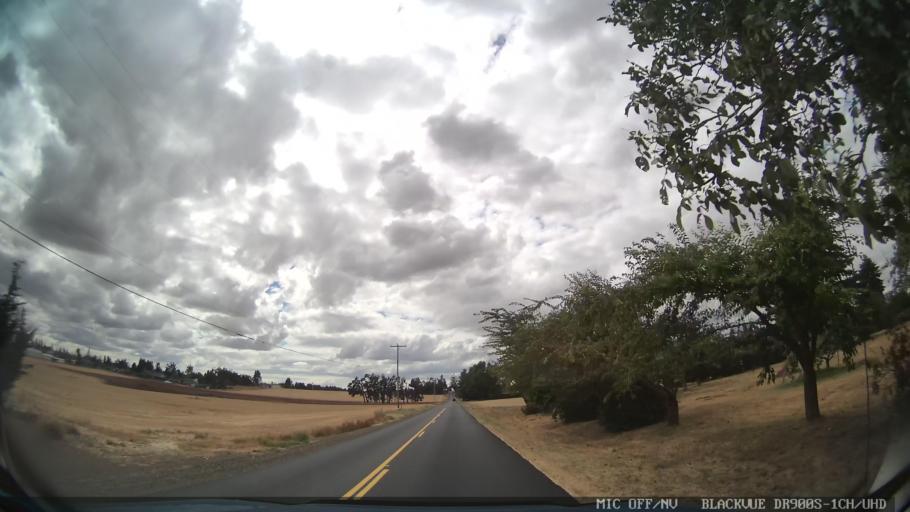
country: US
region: Oregon
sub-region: Marion County
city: Sublimity
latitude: 44.8405
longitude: -122.7795
